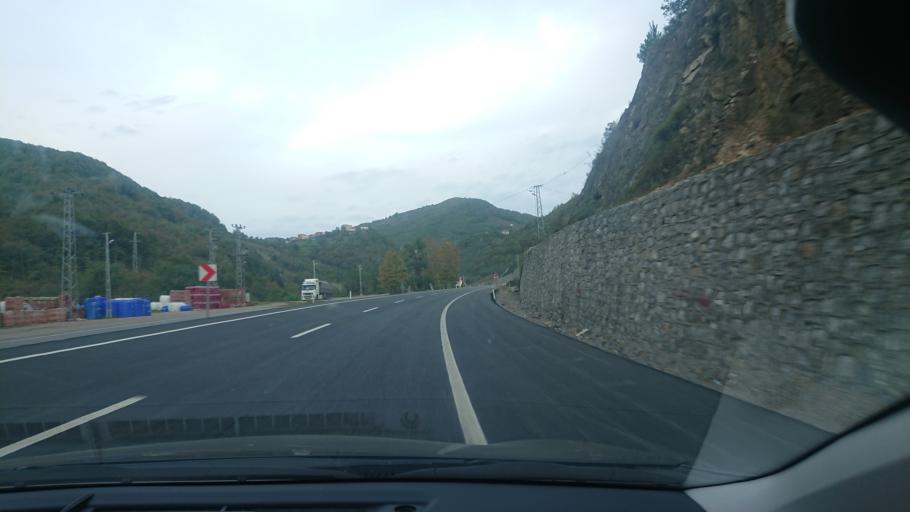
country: TR
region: Zonguldak
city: Beycuma
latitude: 41.3825
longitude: 31.9445
